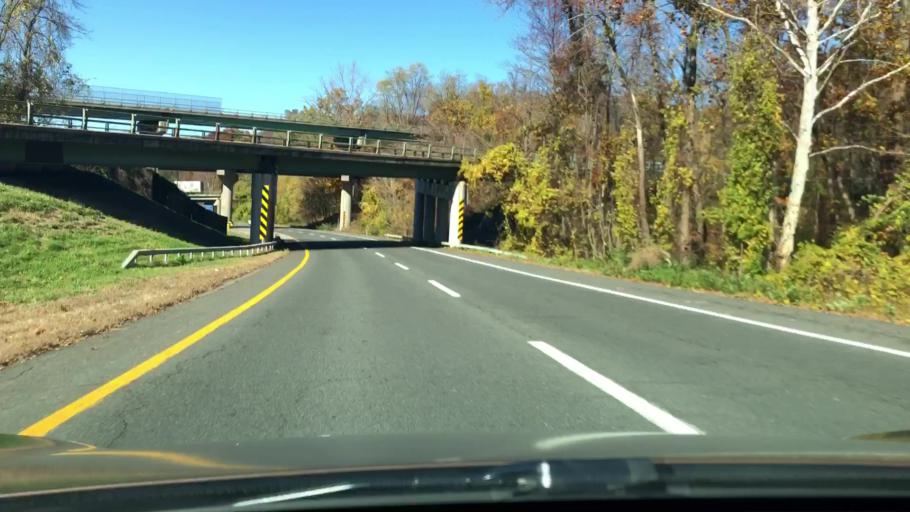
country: US
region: New York
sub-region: Westchester County
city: Purchase
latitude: 41.0251
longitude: -73.7292
